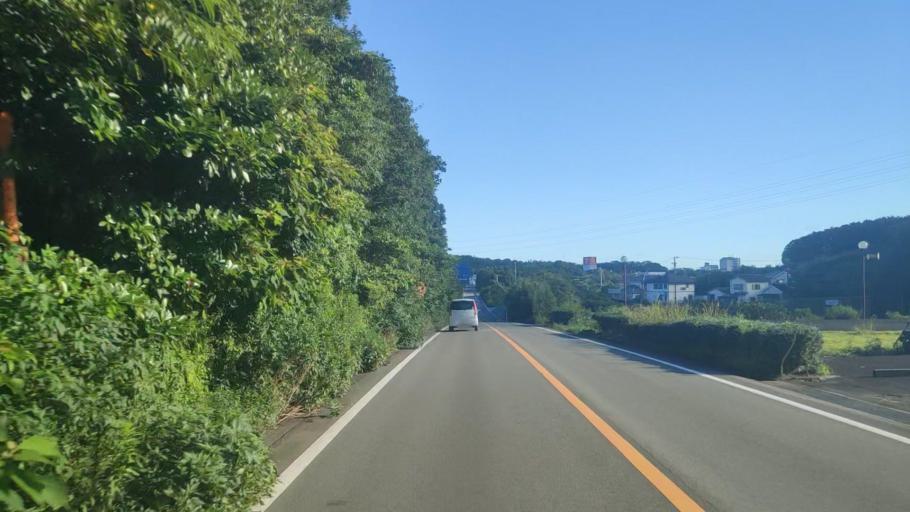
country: JP
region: Mie
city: Toba
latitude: 34.3335
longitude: 136.8405
